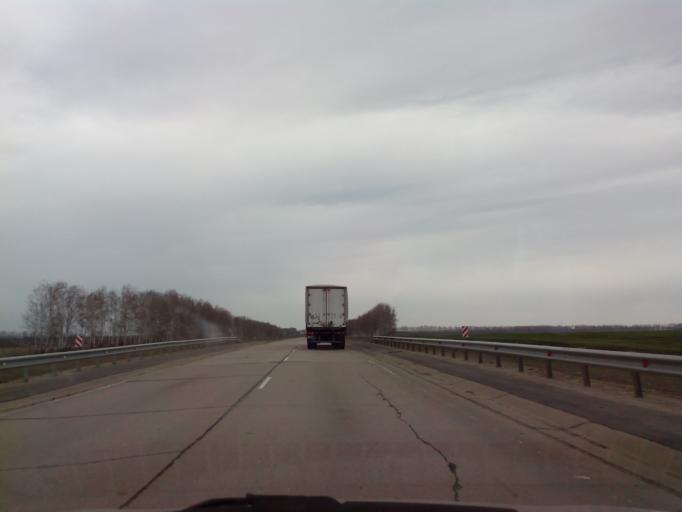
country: RU
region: Tambov
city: Pokrovo-Prigorodnoye
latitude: 52.6471
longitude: 41.3410
